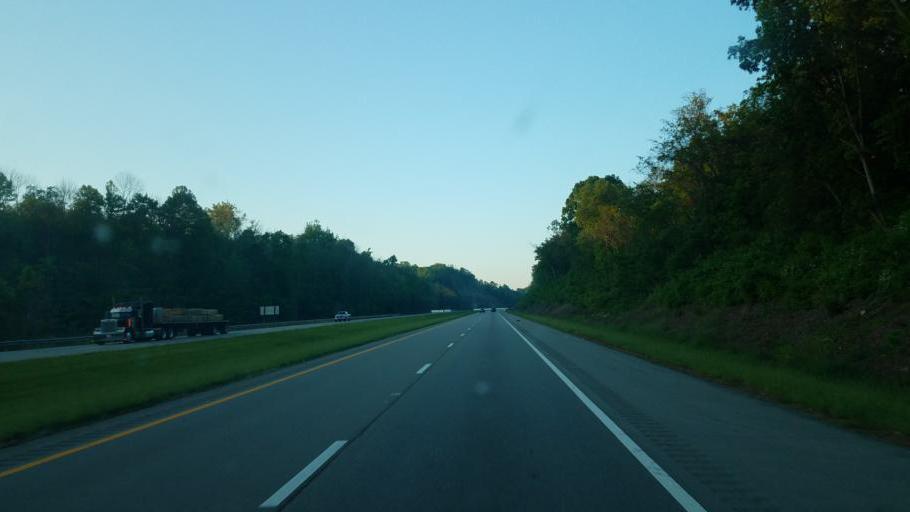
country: US
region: Ohio
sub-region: Noble County
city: Caldwell
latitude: 39.6168
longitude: -81.4590
